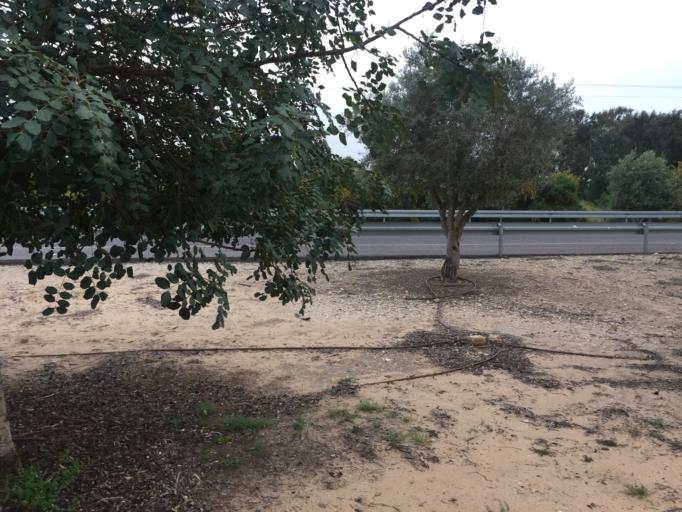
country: IL
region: Haifa
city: Qesarya
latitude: 32.5044
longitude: 34.9100
